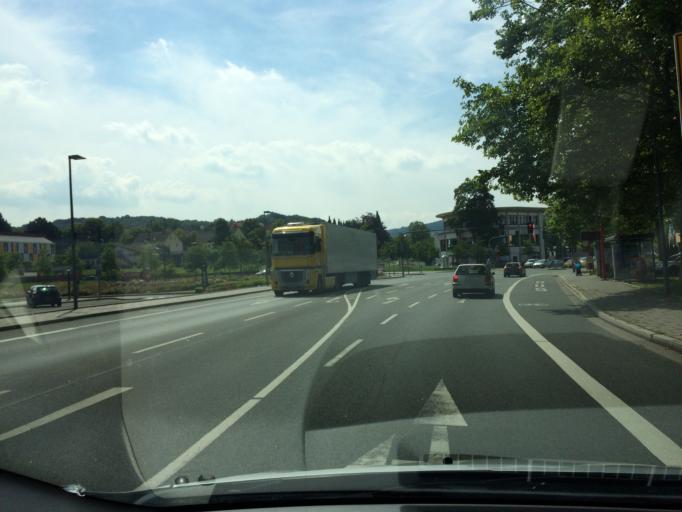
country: DE
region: North Rhine-Westphalia
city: Hemer
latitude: 51.3863
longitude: 7.7682
